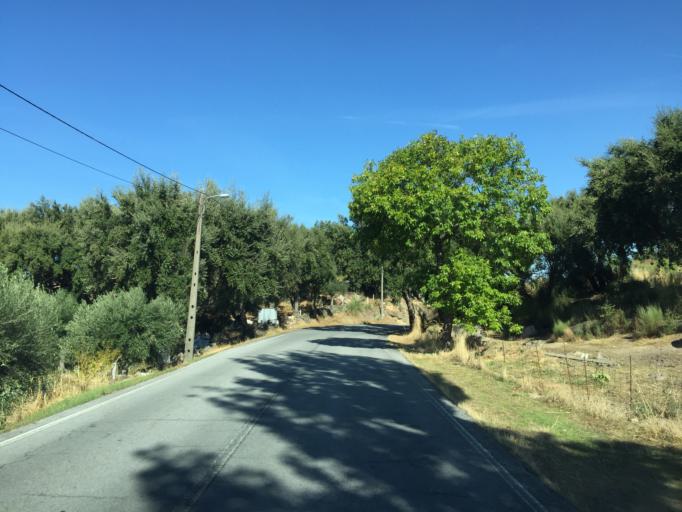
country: PT
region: Portalegre
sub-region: Marvao
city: Marvao
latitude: 39.4408
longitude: -7.3670
